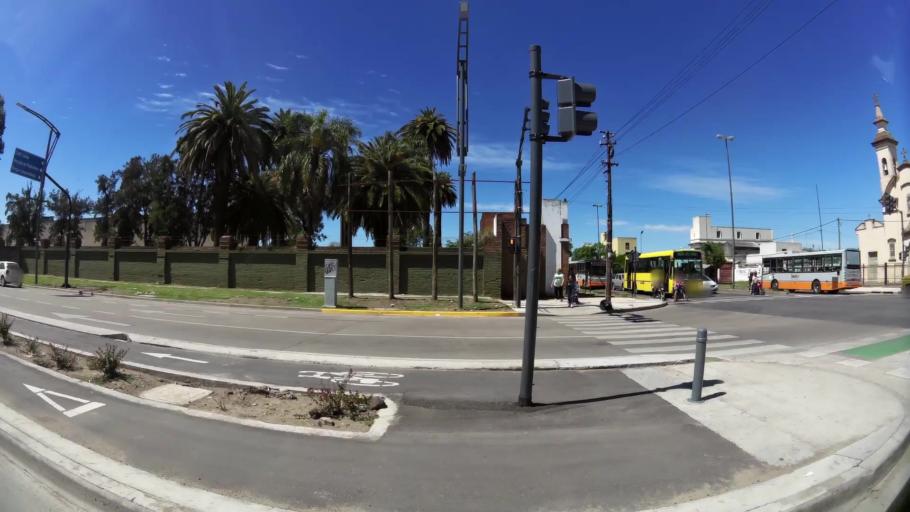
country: AR
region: Santa Fe
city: Perez
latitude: -32.9594
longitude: -60.7117
